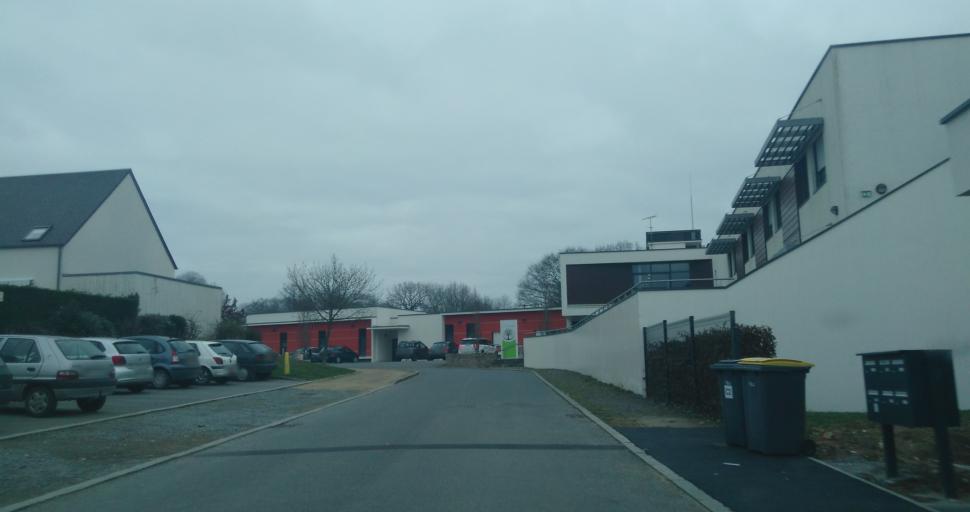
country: FR
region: Brittany
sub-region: Departement d'Ille-et-Vilaine
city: Romille
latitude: 48.2158
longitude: -1.8957
